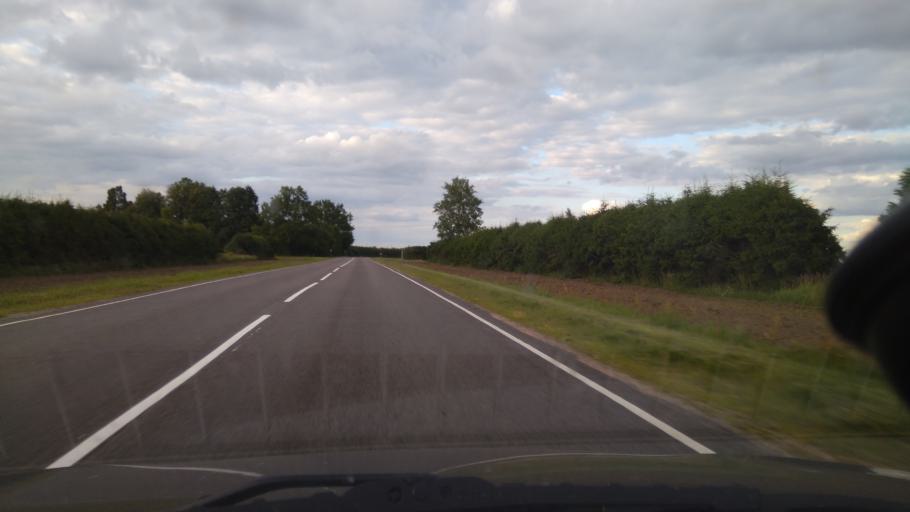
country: BY
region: Grodnenskaya
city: Shchuchin
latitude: 53.5097
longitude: 24.6858
